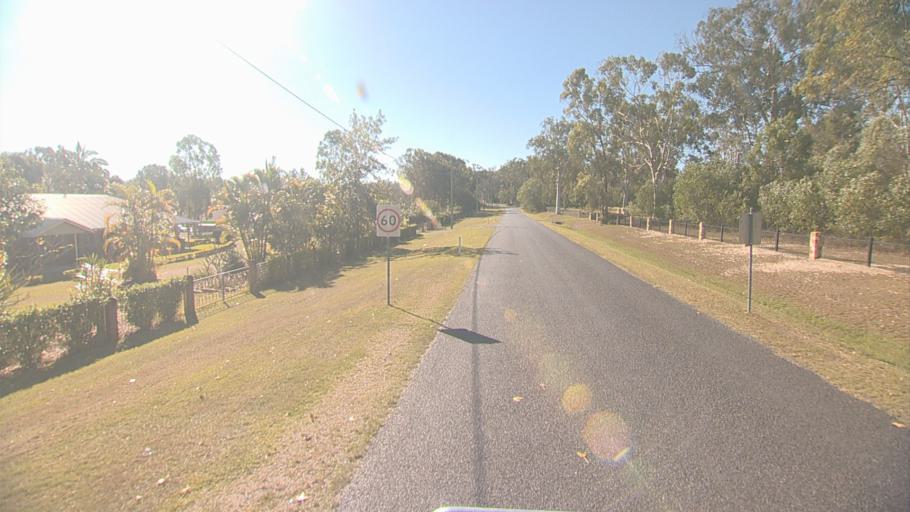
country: AU
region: Queensland
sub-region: Logan
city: Chambers Flat
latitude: -27.7369
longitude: 153.0777
